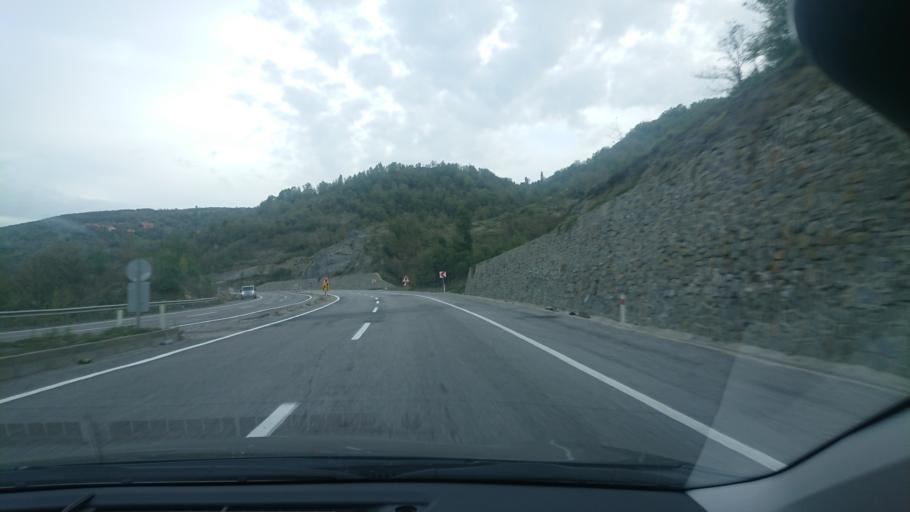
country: TR
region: Zonguldak
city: Beycuma
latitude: 41.3985
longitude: 31.9371
